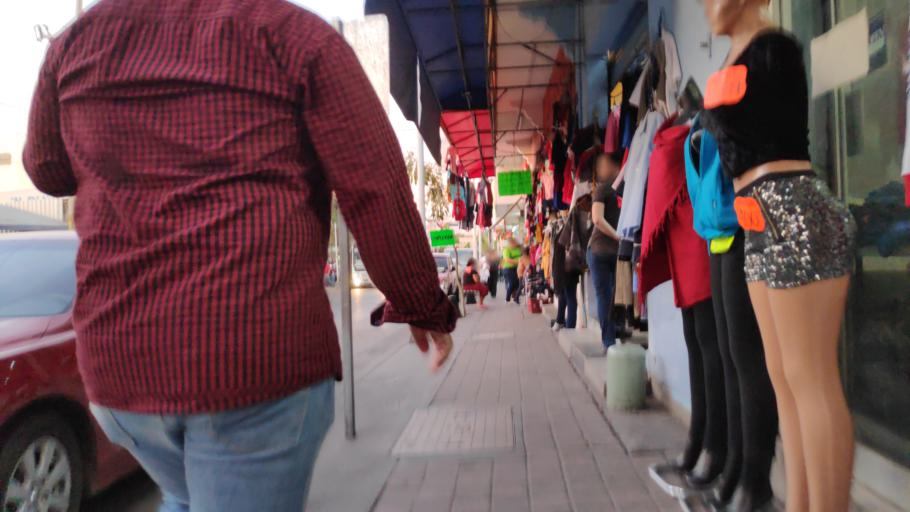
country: MX
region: Sinaloa
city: Culiacan
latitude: 24.8057
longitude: -107.3962
